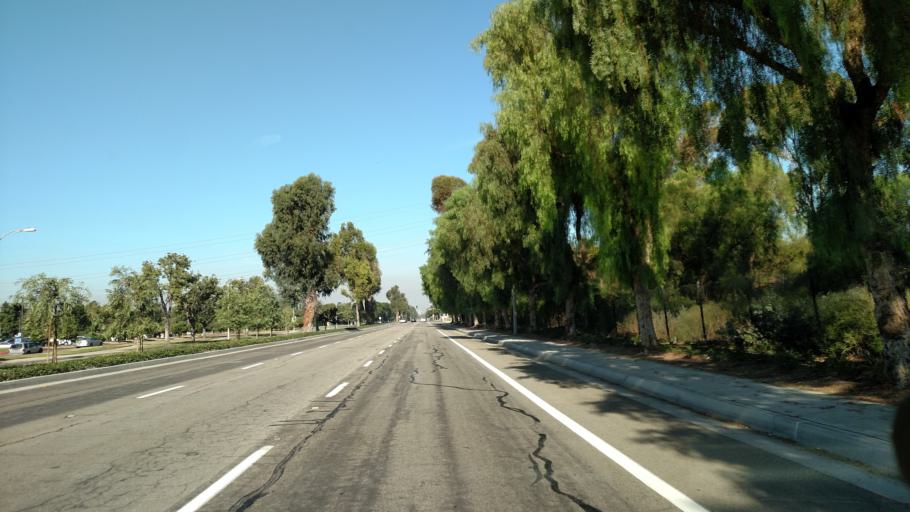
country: US
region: California
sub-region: Orange County
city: Irvine
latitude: 33.6780
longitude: -117.7762
